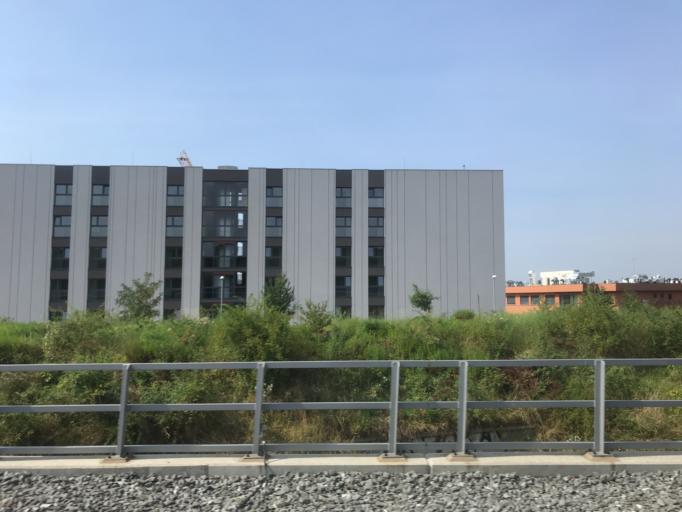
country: CZ
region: Praha
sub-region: Praha 14
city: Hostavice
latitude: 50.0560
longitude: 14.5259
